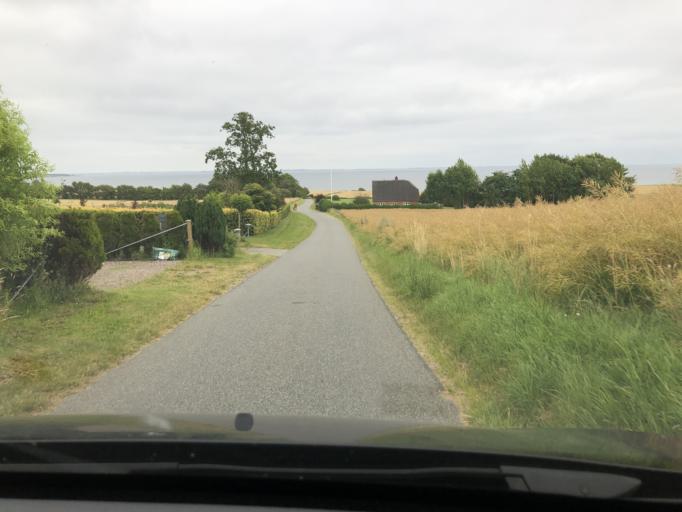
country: DK
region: South Denmark
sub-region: AEro Kommune
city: AEroskobing
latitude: 54.8321
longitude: 10.4295
